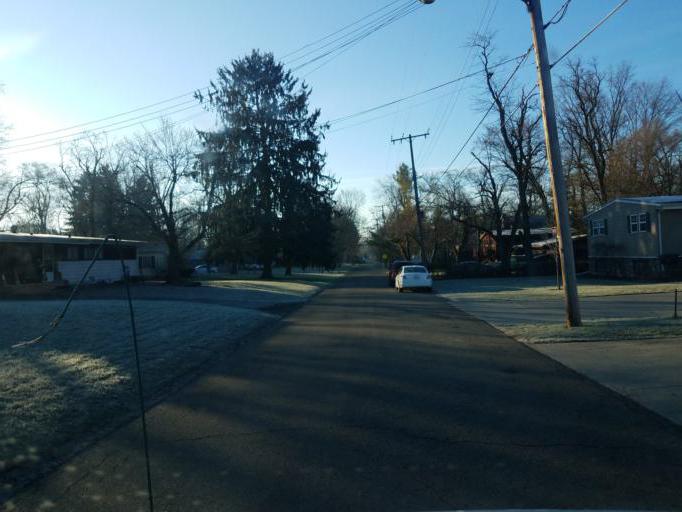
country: US
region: Ohio
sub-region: Marion County
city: Marion
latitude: 40.5798
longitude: -83.1163
